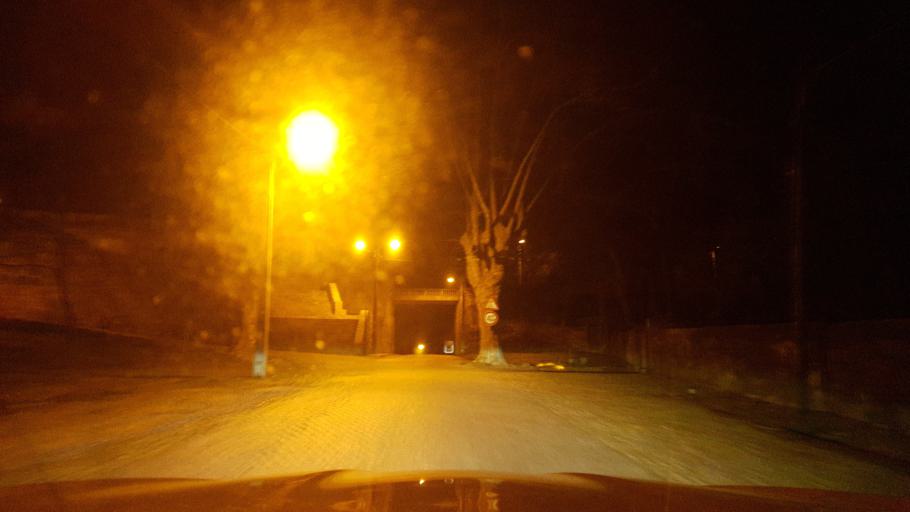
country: PT
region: Porto
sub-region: Matosinhos
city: Guifoes
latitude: 41.2188
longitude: -8.6632
